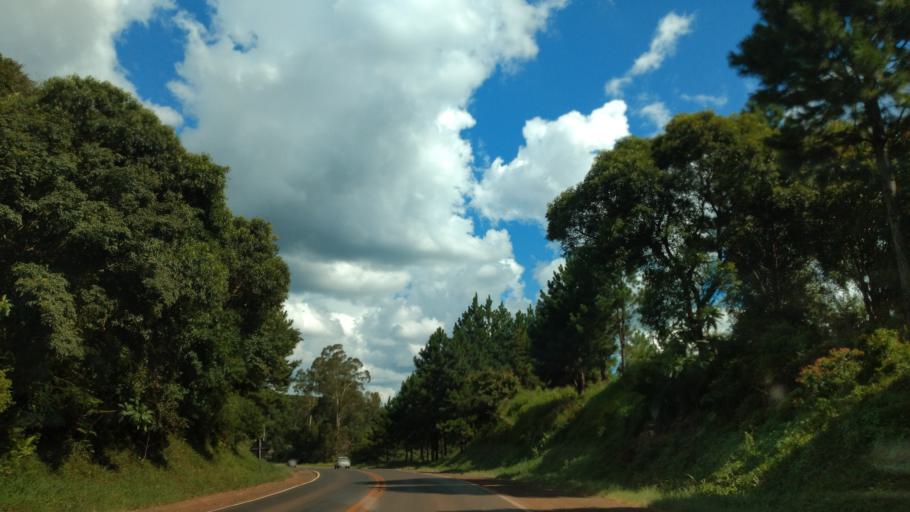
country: BR
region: Parana
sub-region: Guarapuava
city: Guarapuava
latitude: -25.4207
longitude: -51.4929
